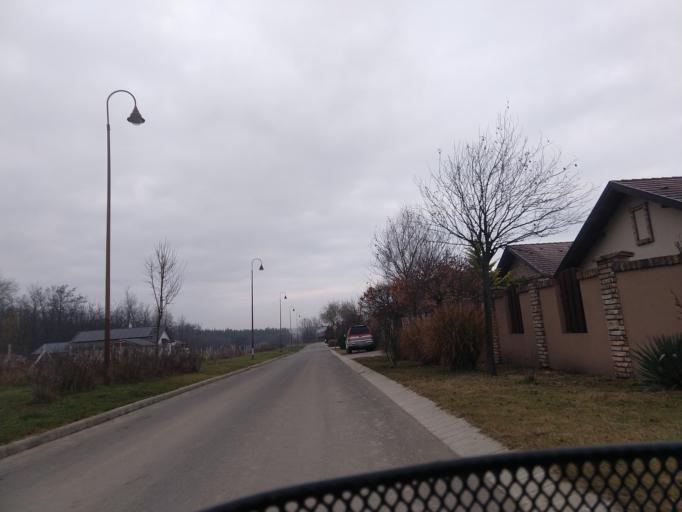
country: HU
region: Pest
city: Orbottyan
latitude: 47.6648
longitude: 19.2585
